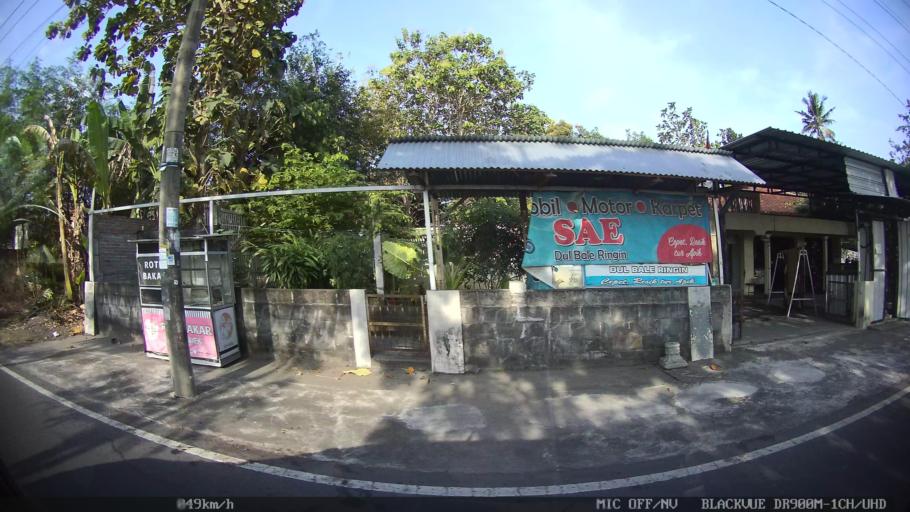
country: ID
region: Daerah Istimewa Yogyakarta
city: Bantul
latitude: -7.8869
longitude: 110.3179
